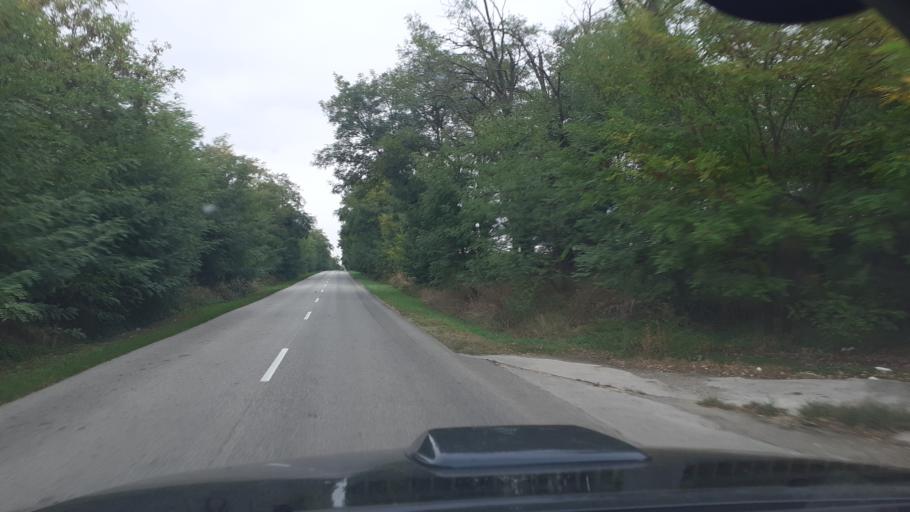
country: HU
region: Fejer
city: Baracs
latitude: 46.8463
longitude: 18.8879
